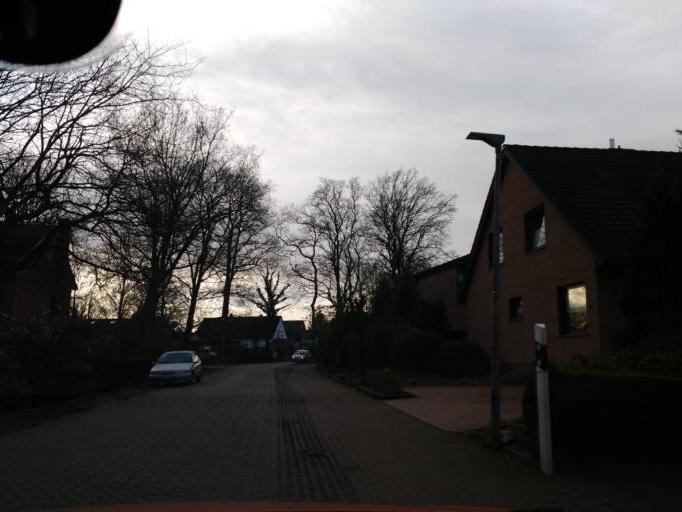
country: DE
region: Lower Saxony
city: Hude
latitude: 53.1029
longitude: 8.4675
